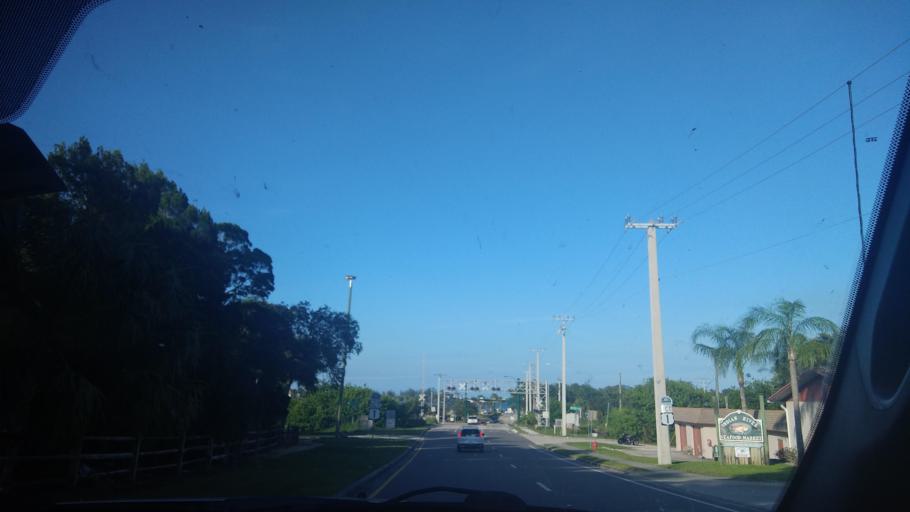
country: US
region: Florida
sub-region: Indian River County
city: Sebastian
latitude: 27.8082
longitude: -80.4680
